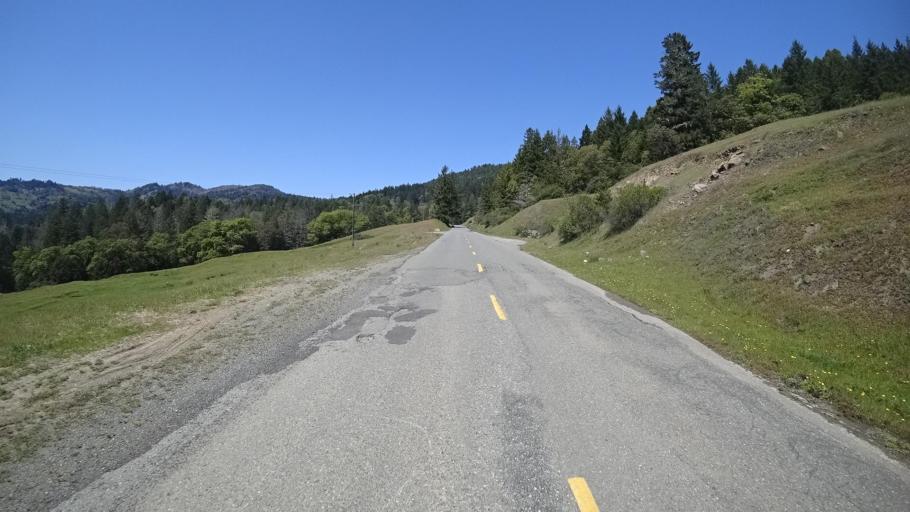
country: US
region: California
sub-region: Humboldt County
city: Redway
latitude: 40.1212
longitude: -123.6477
